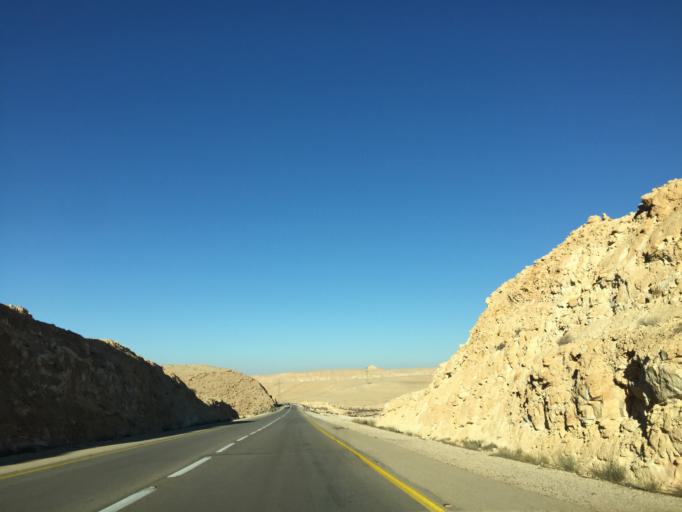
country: IL
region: Southern District
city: Midreshet Ben-Gurion
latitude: 30.7532
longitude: 34.7698
